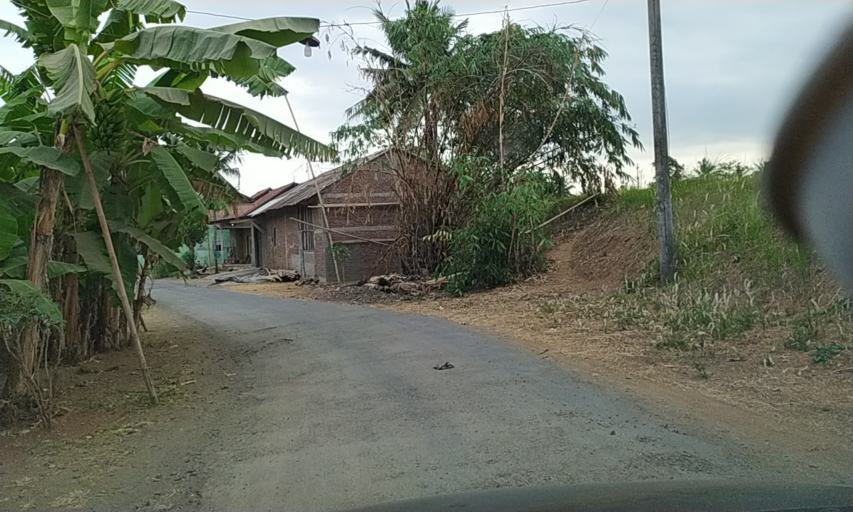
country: ID
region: Central Java
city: Bojongsari
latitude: -7.3197
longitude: 108.7640
